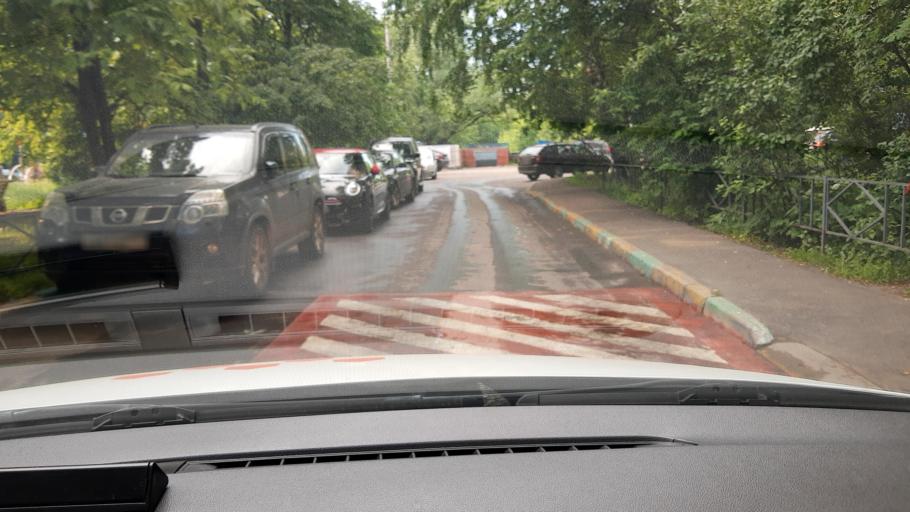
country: RU
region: Moscow
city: Veshnyaki
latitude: 55.7245
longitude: 37.8214
